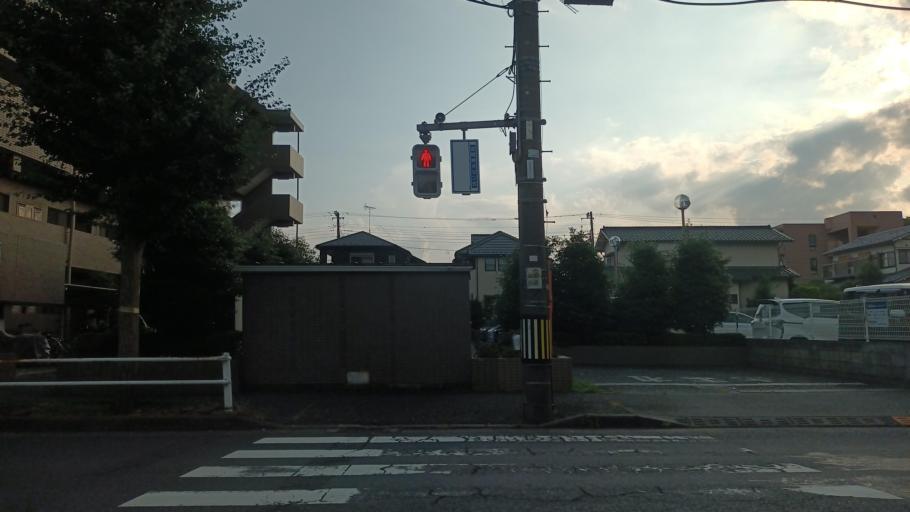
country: JP
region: Tokyo
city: Fussa
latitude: 35.7654
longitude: 139.3130
